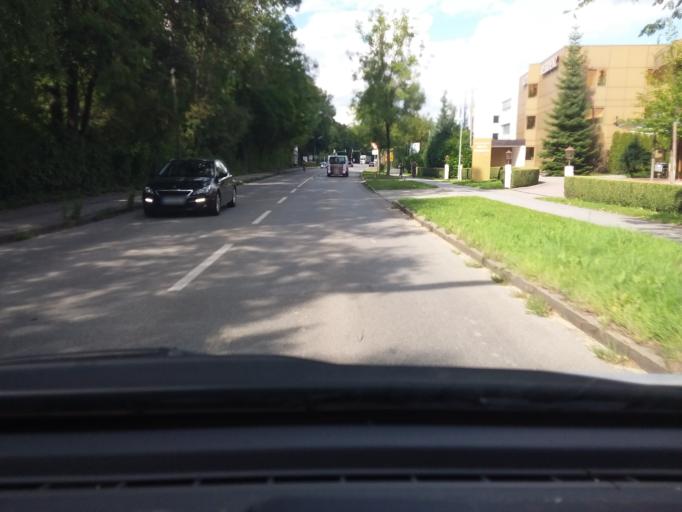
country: DE
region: Bavaria
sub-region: Upper Bavaria
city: Ismaning
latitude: 48.2355
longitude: 11.6781
